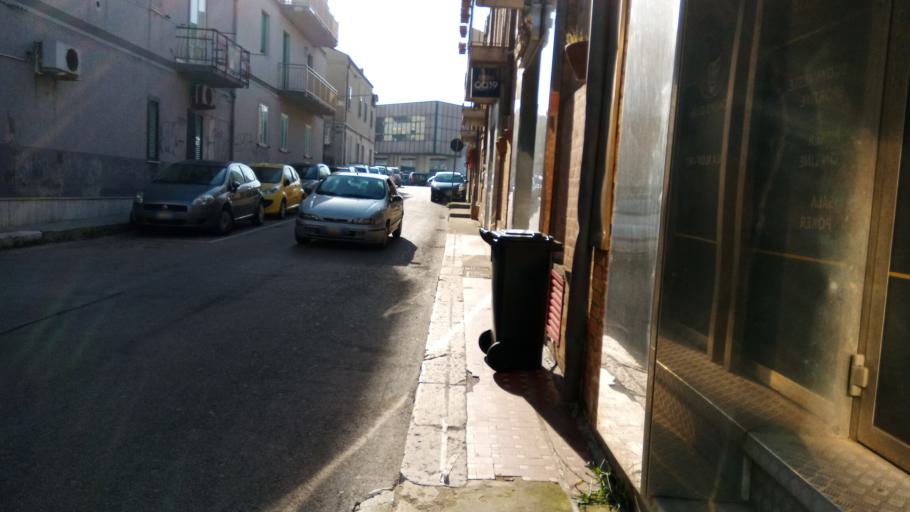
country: IT
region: Molise
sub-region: Provincia di Campobasso
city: Termoli
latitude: 42.0028
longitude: 14.9919
